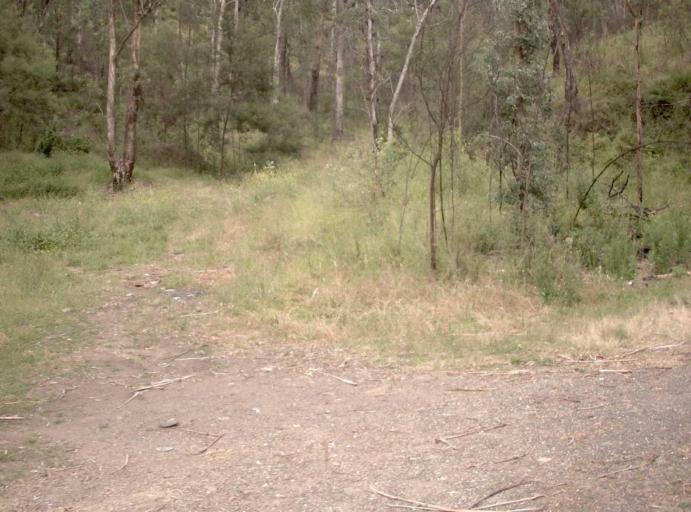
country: AU
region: Victoria
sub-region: Wellington
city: Heyfield
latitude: -37.7886
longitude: 146.6700
